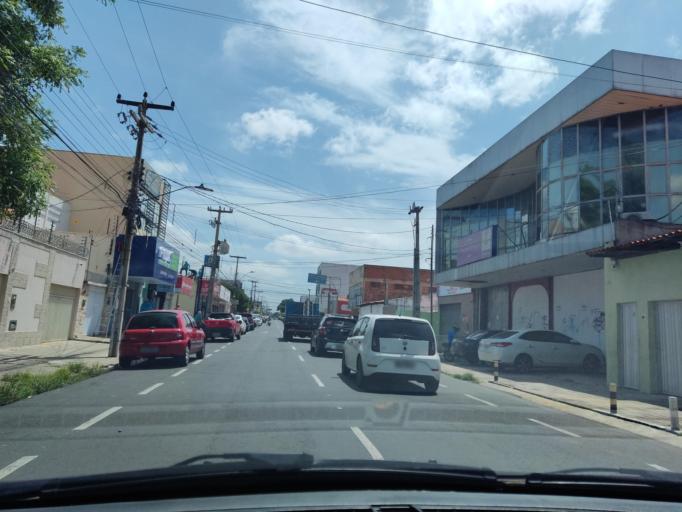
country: BR
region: Piaui
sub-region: Teresina
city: Teresina
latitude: -5.0848
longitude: -42.8167
